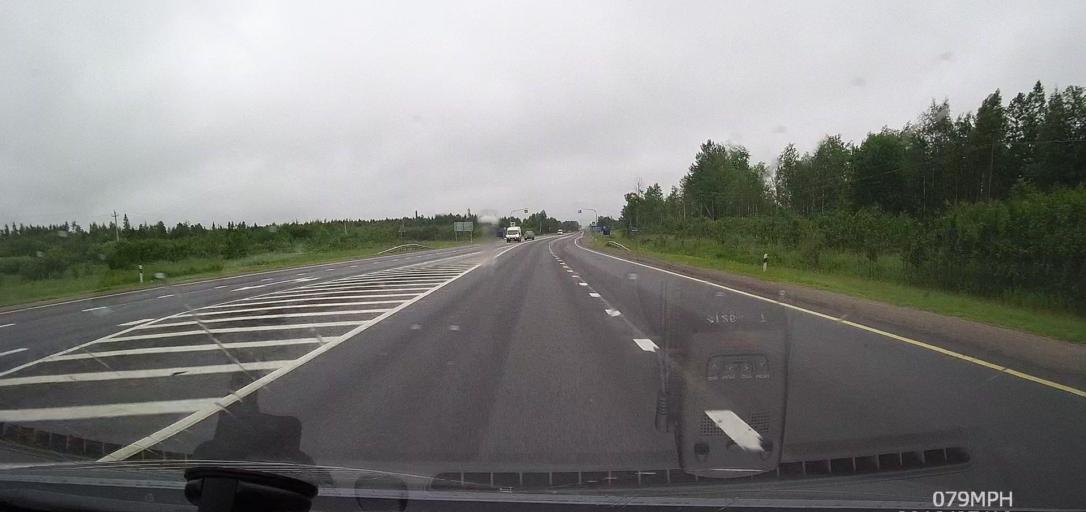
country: RU
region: Leningrad
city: Staraya Ladoga
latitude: 59.9974
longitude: 32.1035
